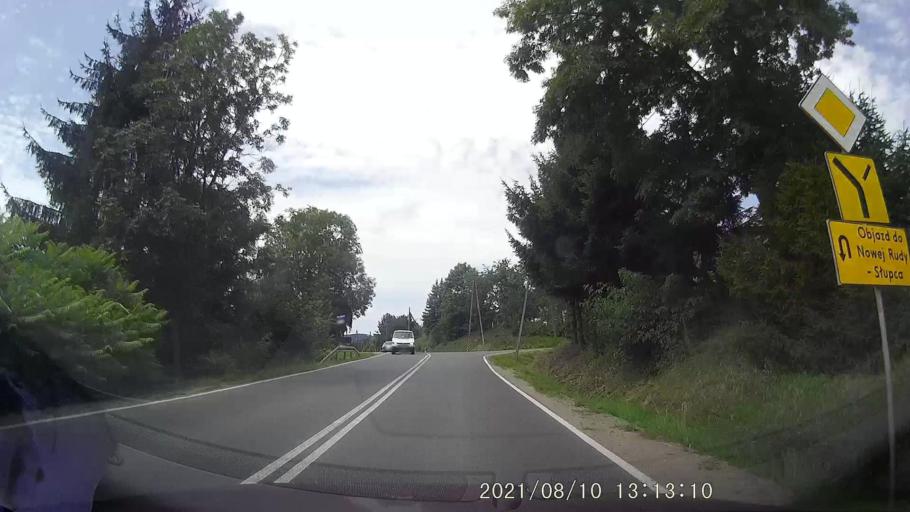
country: PL
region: Lower Silesian Voivodeship
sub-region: Powiat klodzki
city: Nowa Ruda
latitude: 50.5188
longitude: 16.5050
